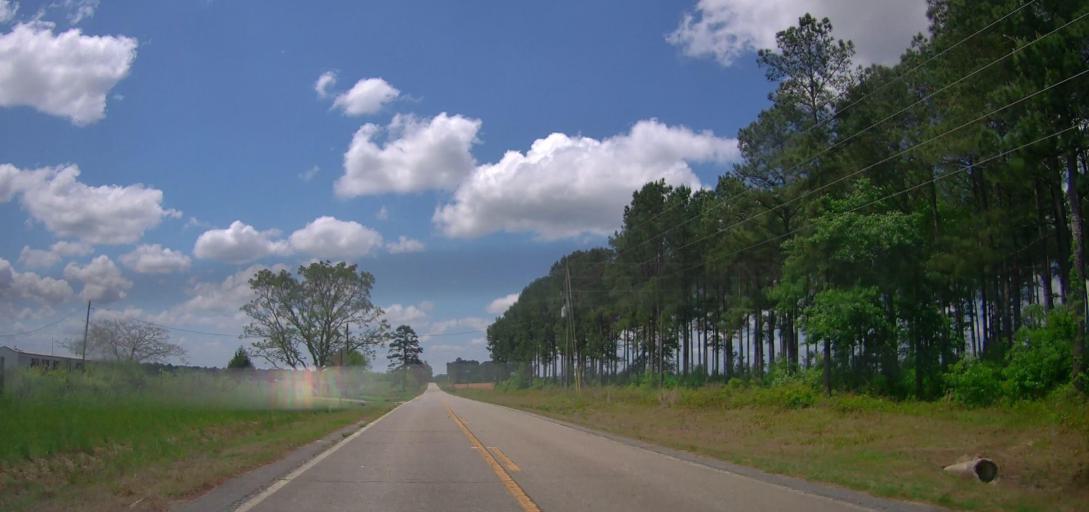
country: US
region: Georgia
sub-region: Dodge County
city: Chester
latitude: 32.5201
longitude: -83.2170
